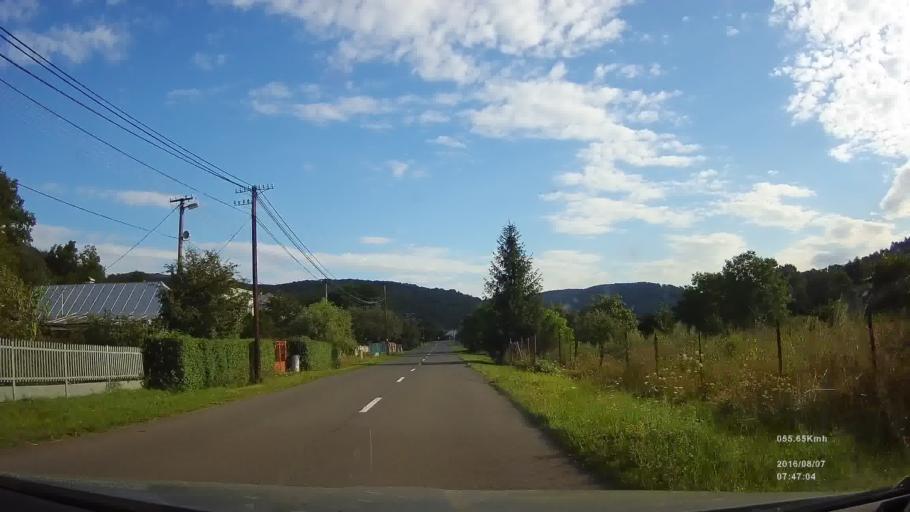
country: SK
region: Presovsky
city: Stropkov
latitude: 49.2762
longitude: 21.7518
